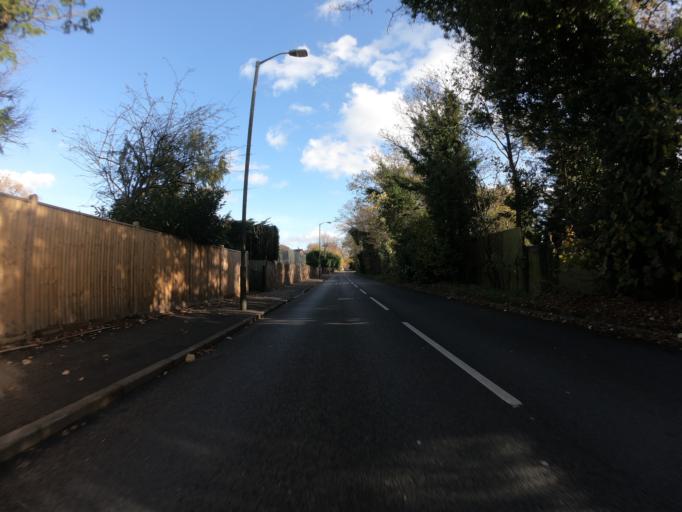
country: GB
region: England
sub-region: Greater London
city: Orpington
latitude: 51.4001
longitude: 0.0917
